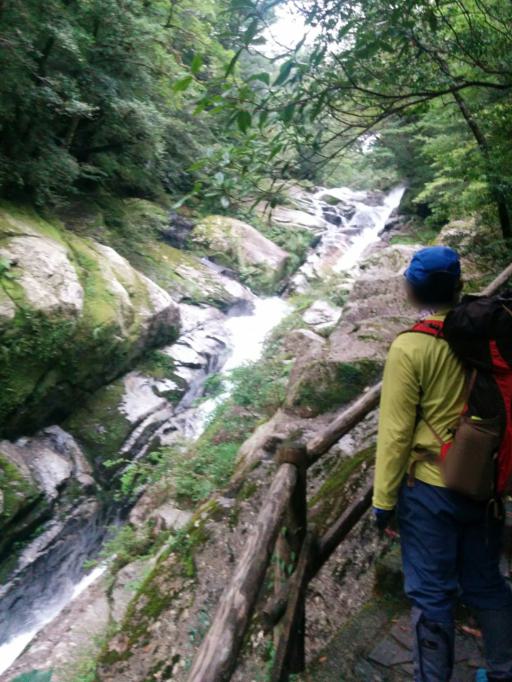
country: JP
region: Kagoshima
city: Nishinoomote
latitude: 30.3780
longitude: 130.5734
